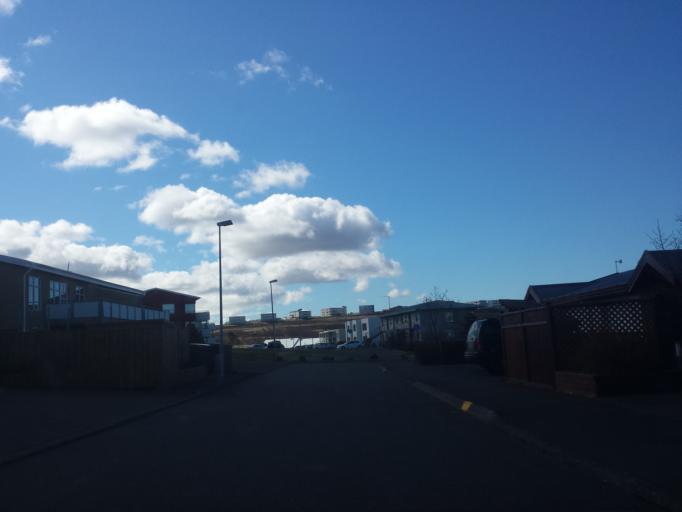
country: IS
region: Capital Region
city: Reykjavik
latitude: 64.0924
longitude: -21.8510
